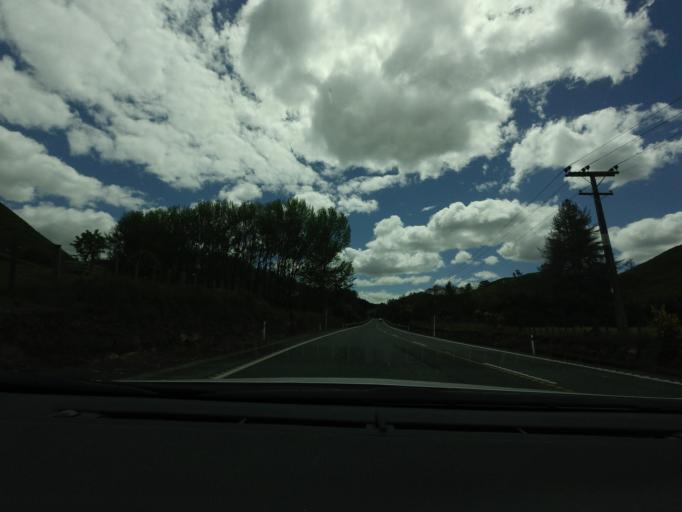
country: NZ
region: Bay of Plenty
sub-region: Rotorua District
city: Rotorua
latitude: -38.2990
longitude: 176.3623
